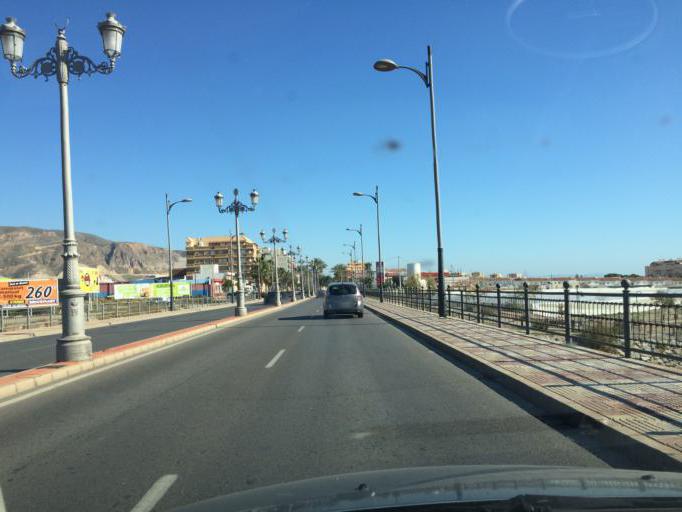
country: ES
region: Andalusia
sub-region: Provincia de Almeria
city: Aguadulce
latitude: 36.8092
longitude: -2.5957
